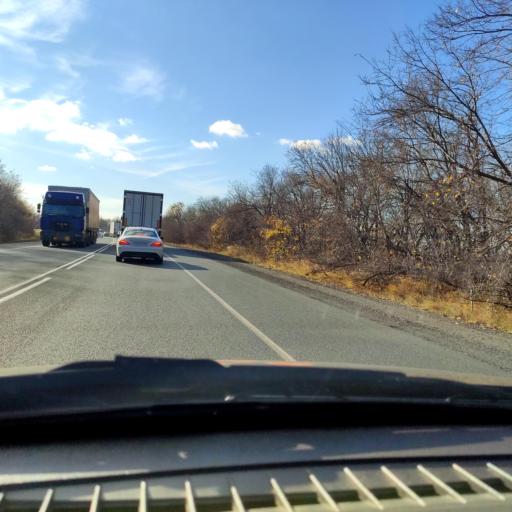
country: RU
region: Samara
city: Zhigulevsk
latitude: 53.3224
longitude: 49.3751
